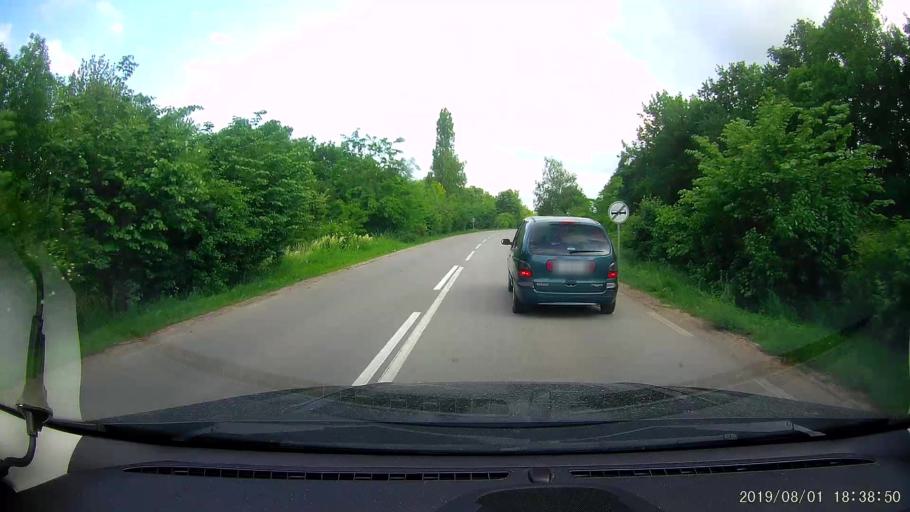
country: BG
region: Shumen
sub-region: Obshtina Khitrino
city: Gara Khitrino
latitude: 43.3970
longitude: 26.9168
